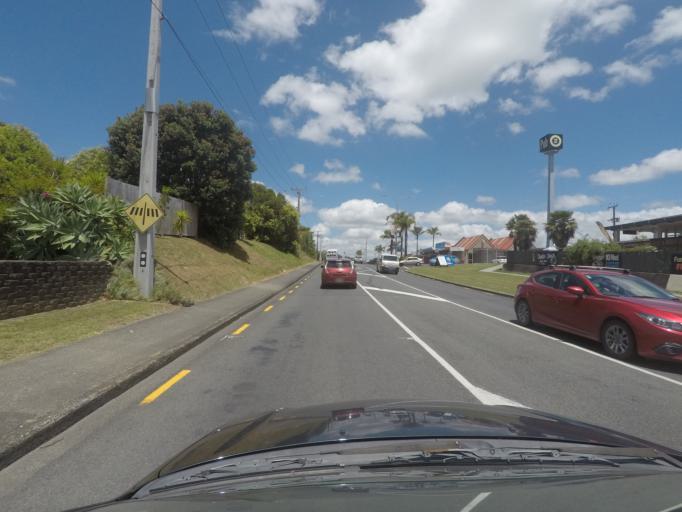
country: NZ
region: Northland
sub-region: Whangarei
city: Whangarei
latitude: -35.7538
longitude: 174.3683
